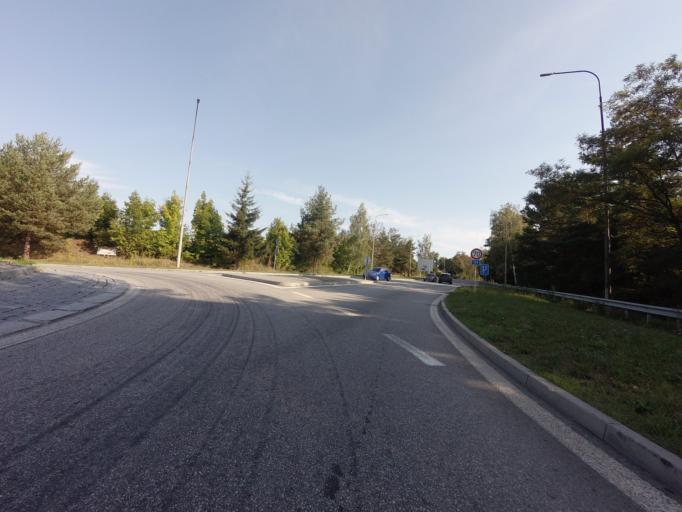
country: CZ
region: Jihocesky
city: Tyn nad Vltavou
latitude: 49.2282
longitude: 14.4246
